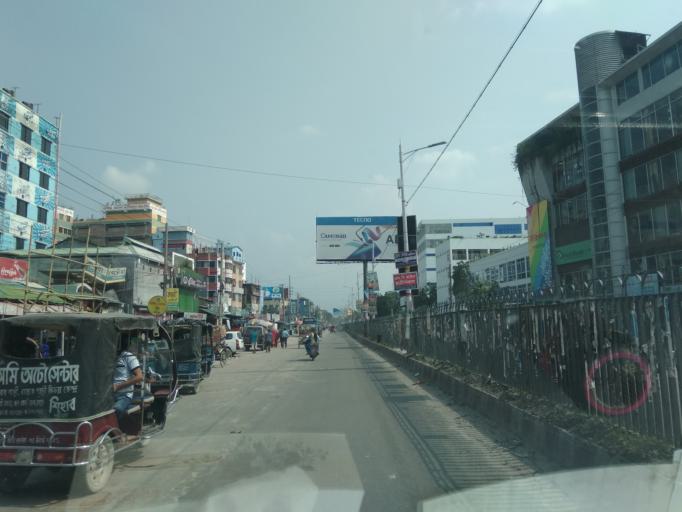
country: BD
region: Rangpur Division
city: Rangpur
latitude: 25.7646
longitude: 89.2313
